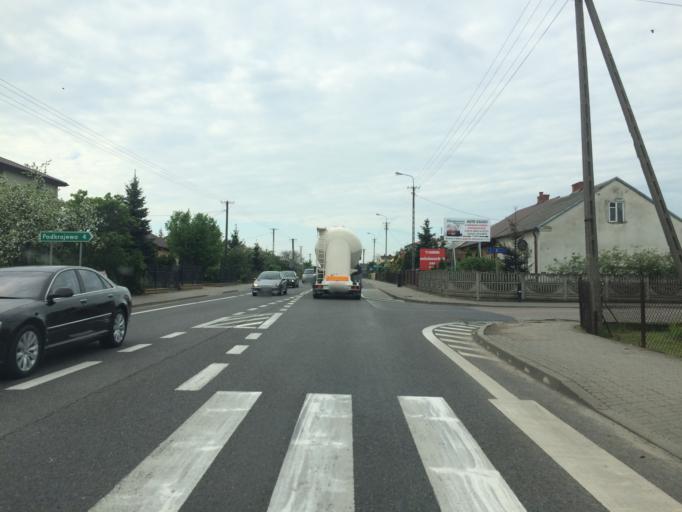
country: PL
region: Masovian Voivodeship
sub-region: Powiat mlawski
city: Wisniewo
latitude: 53.0653
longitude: 20.3483
